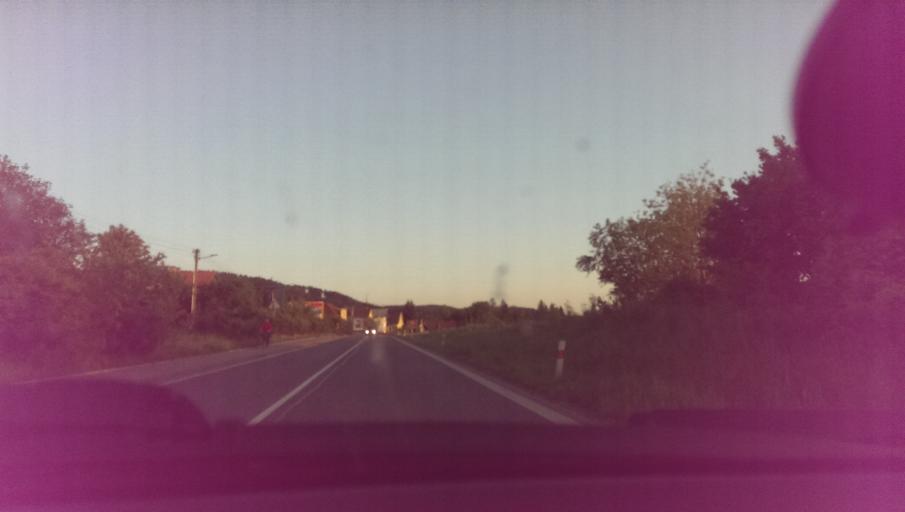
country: CZ
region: Zlin
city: Valasske Mezirici
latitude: 49.4570
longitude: 17.9718
